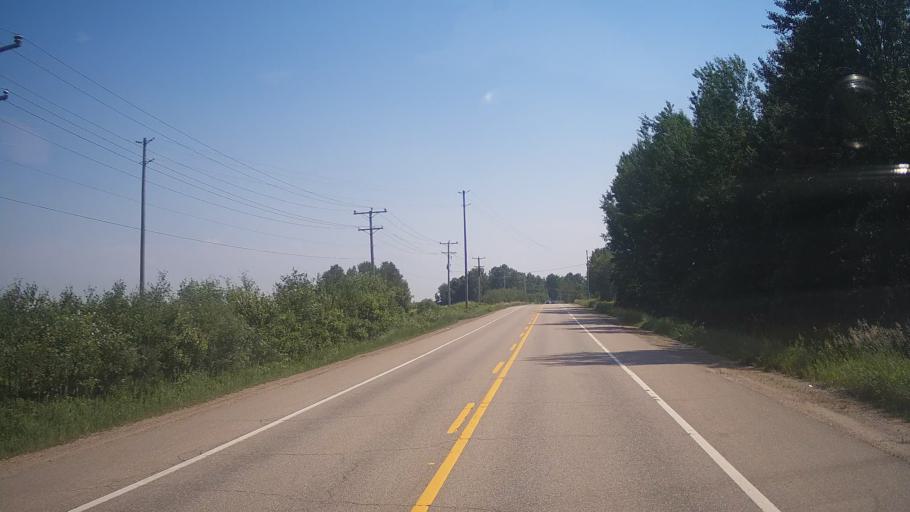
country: CA
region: Ontario
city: Pembroke
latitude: 45.8324
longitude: -77.0134
